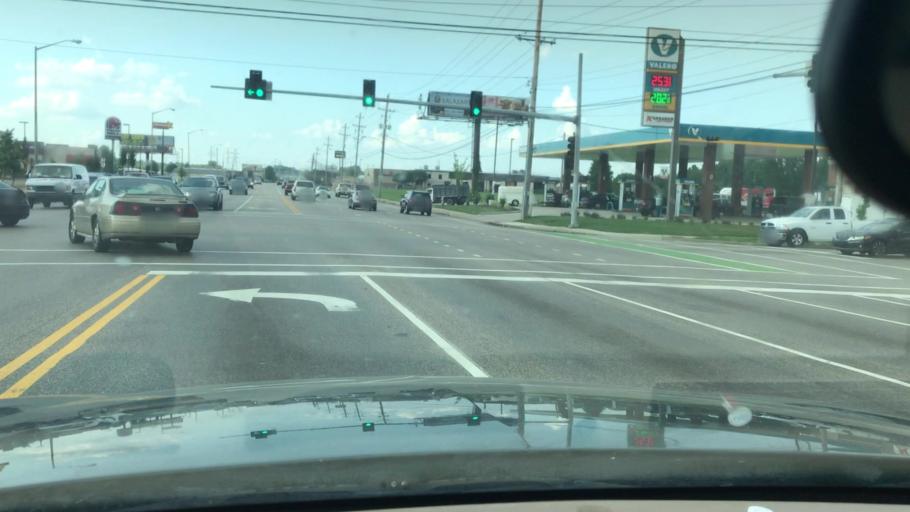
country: US
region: Tennessee
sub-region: Shelby County
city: Bartlett
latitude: 35.1784
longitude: -89.8362
